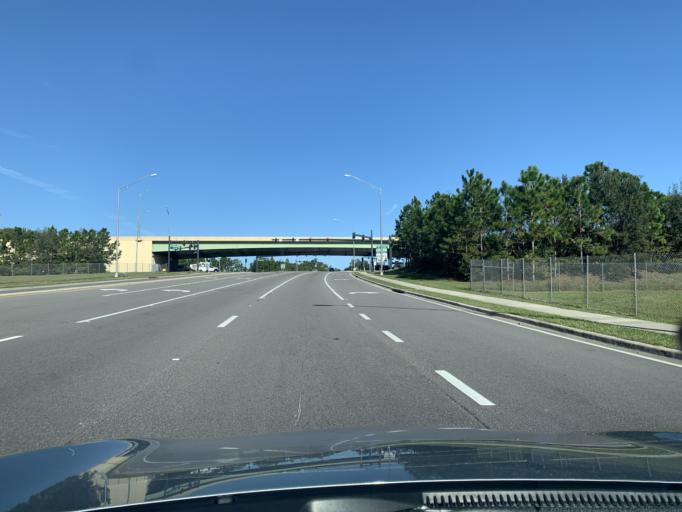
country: US
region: Florida
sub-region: Orange County
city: Clarcona
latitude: 28.6327
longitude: -81.4764
